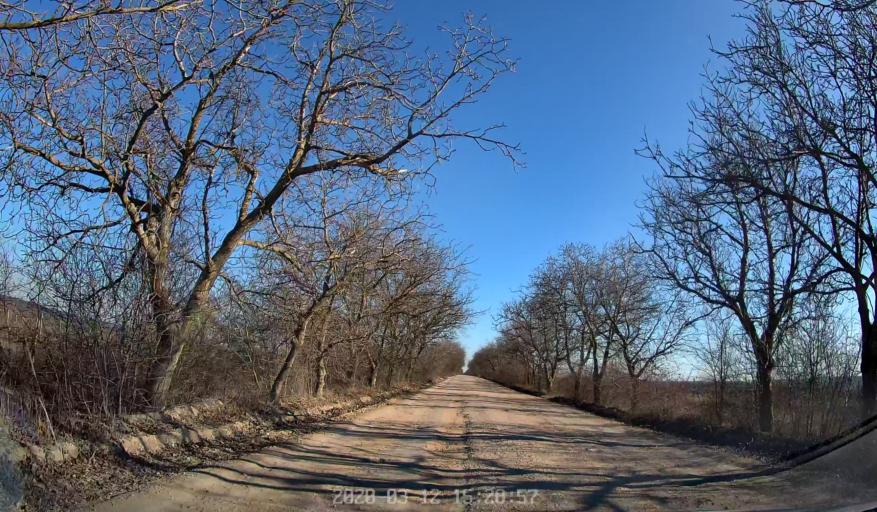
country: MD
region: Chisinau
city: Ciorescu
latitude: 47.1661
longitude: 28.9336
